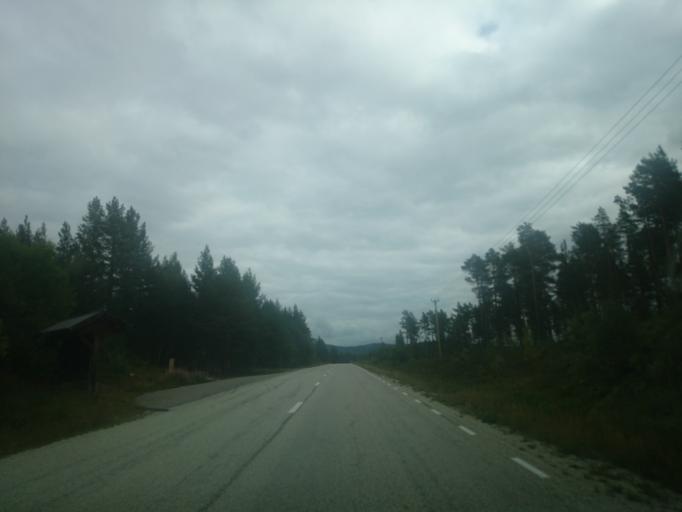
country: SE
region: Jaemtland
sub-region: Harjedalens Kommun
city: Sveg
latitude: 62.4058
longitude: 13.7144
